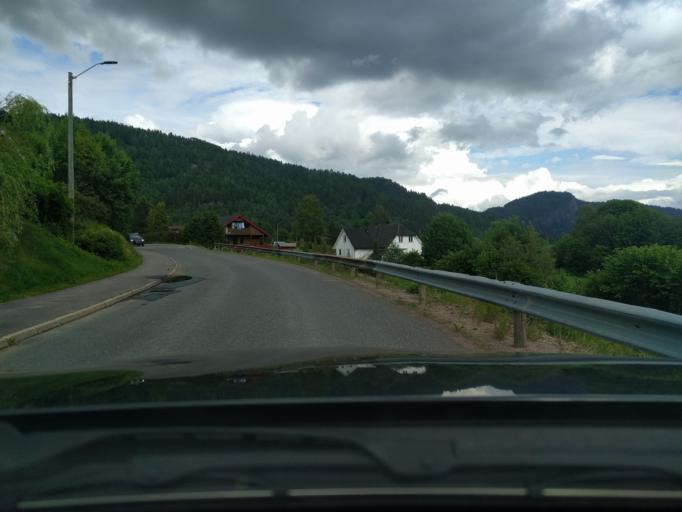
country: NO
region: Telemark
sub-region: Siljan
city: Siljan
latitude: 59.2901
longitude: 9.7130
